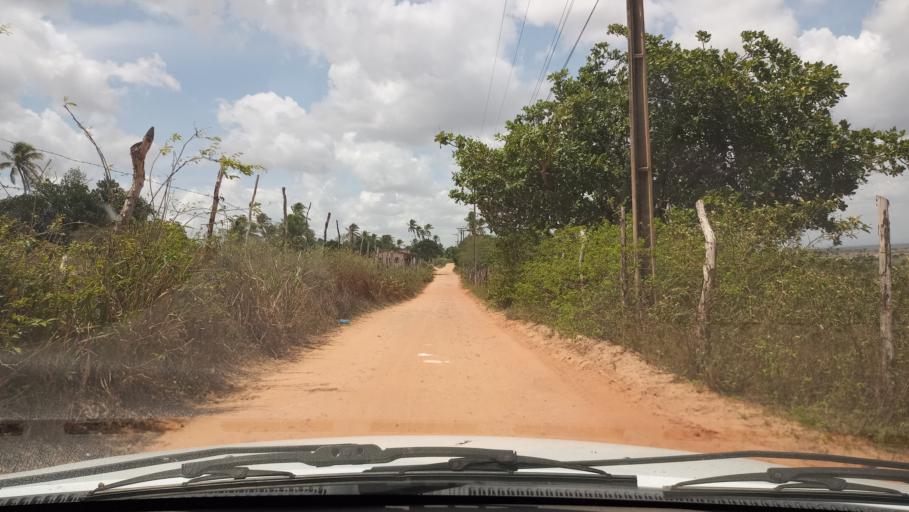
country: BR
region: Rio Grande do Norte
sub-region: Brejinho
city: Brejinho
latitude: -6.2582
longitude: -35.3397
